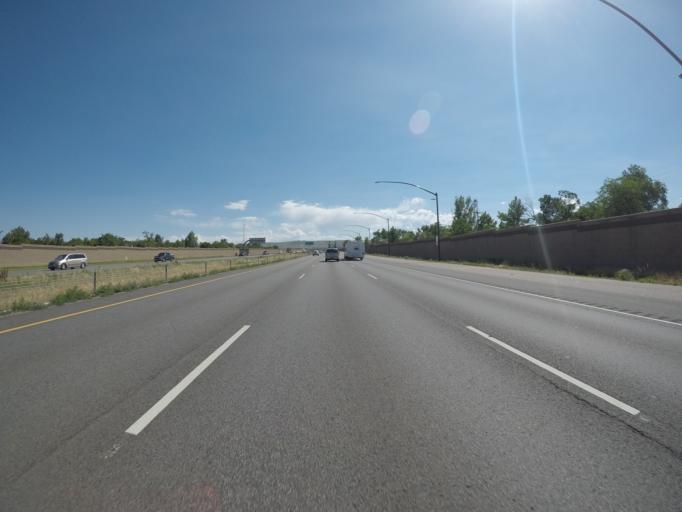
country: US
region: Colorado
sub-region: Jefferson County
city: Applewood
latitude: 39.7513
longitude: -105.1481
